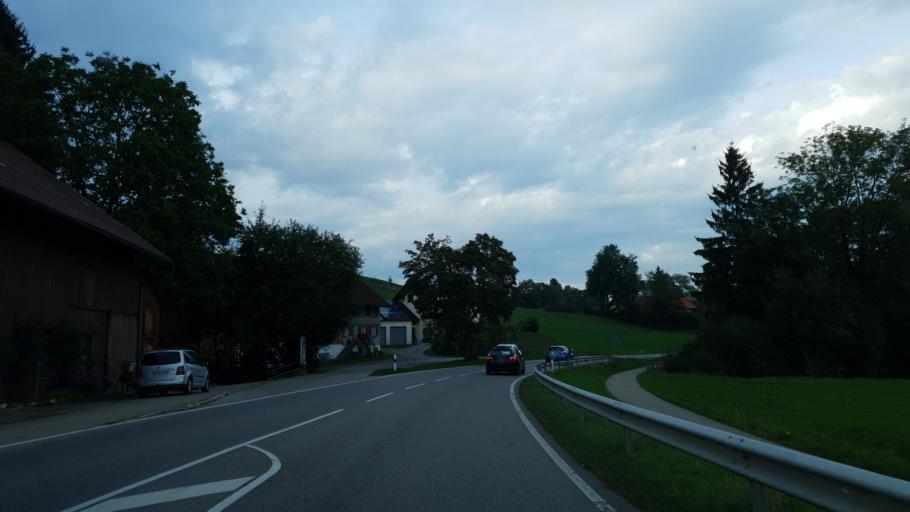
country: DE
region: Bavaria
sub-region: Swabia
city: Gestratz
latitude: 47.6639
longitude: 9.9412
